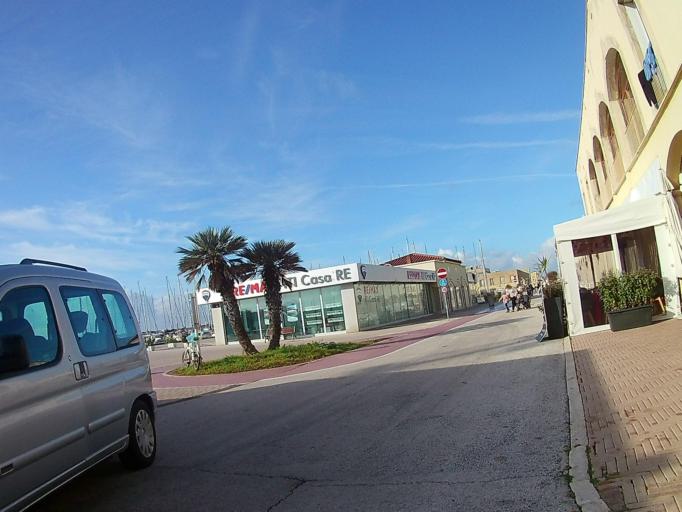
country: IT
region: Latium
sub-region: Citta metropolitana di Roma Capitale
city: Lido di Ostia
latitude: 41.7372
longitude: 12.2525
